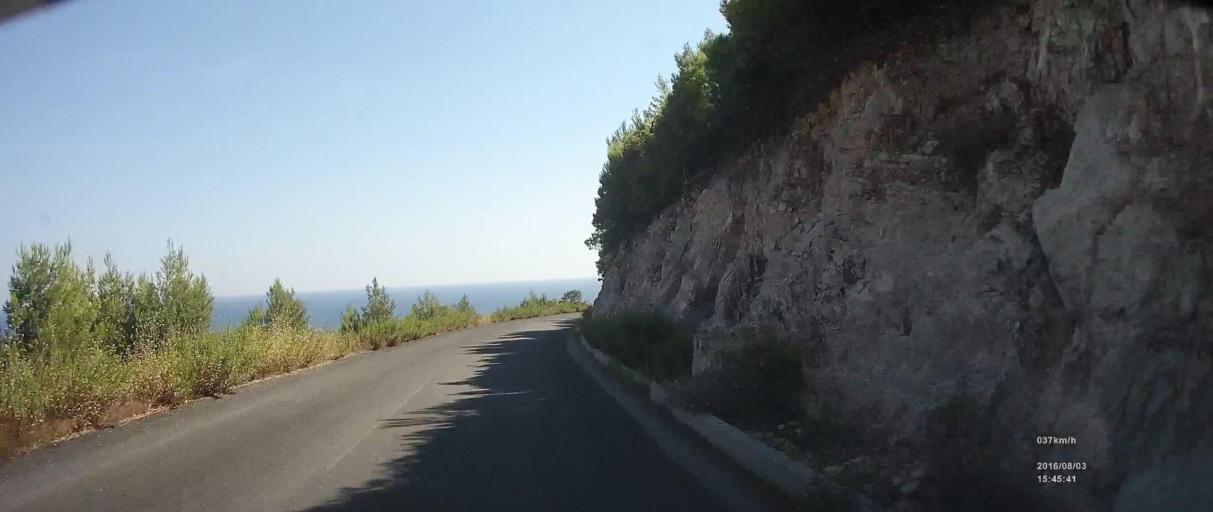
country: HR
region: Dubrovacko-Neretvanska
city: Blato
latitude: 42.7370
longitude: 17.5179
